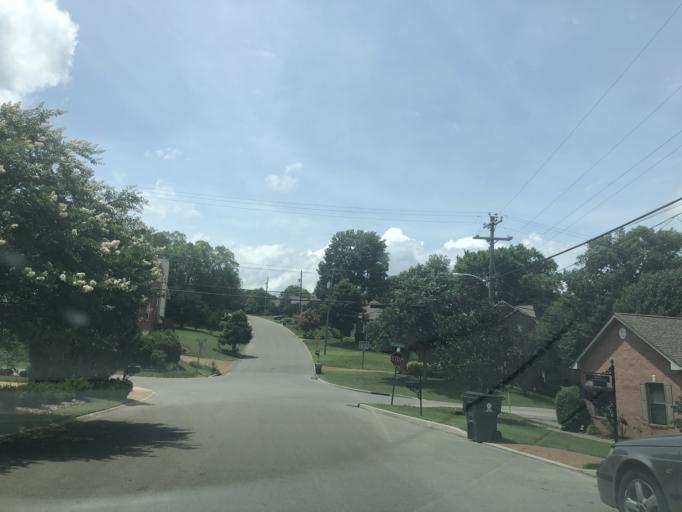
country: US
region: Tennessee
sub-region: Cheatham County
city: Pegram
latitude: 36.0504
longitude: -86.9595
